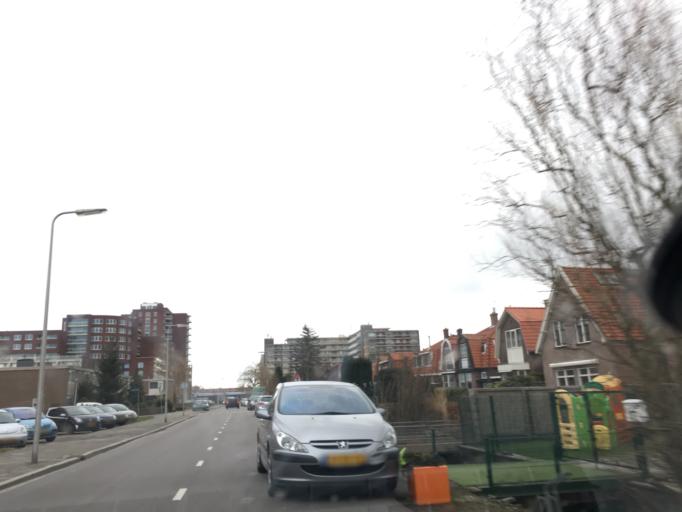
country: NL
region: South Holland
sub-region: Gemeente Krimpen aan den IJssel
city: Krimpen aan den IJssel
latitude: 51.9280
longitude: 4.5939
